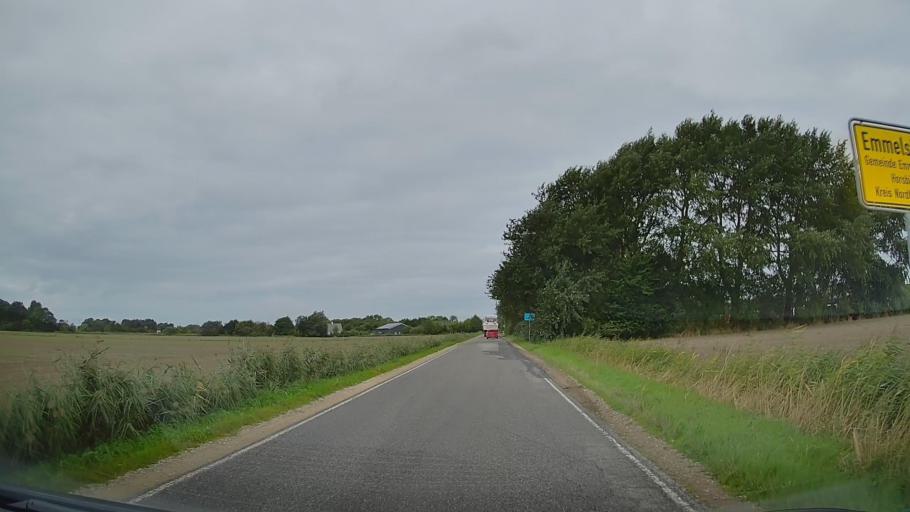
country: DE
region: Schleswig-Holstein
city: Emmelsbull-Horsbull
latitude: 54.8068
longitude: 8.7074
